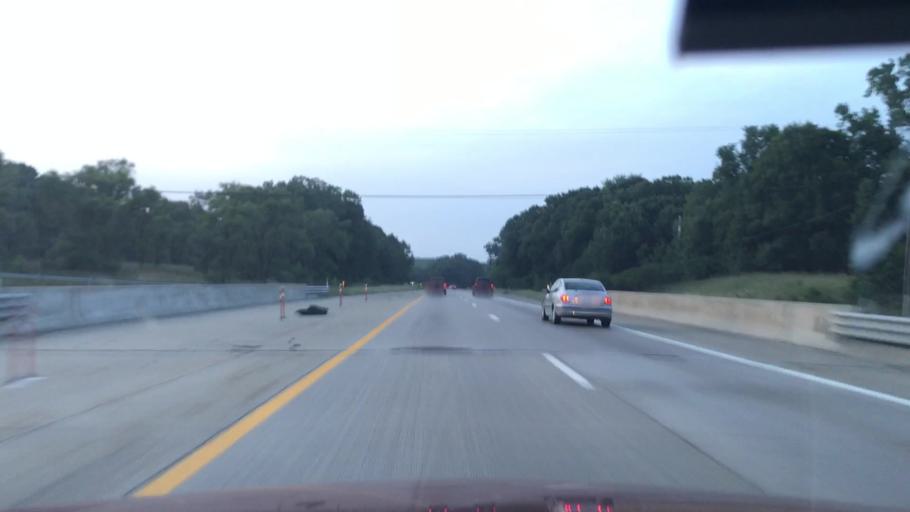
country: US
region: Michigan
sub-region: Kent County
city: Comstock Park
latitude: 43.0577
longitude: -85.6627
